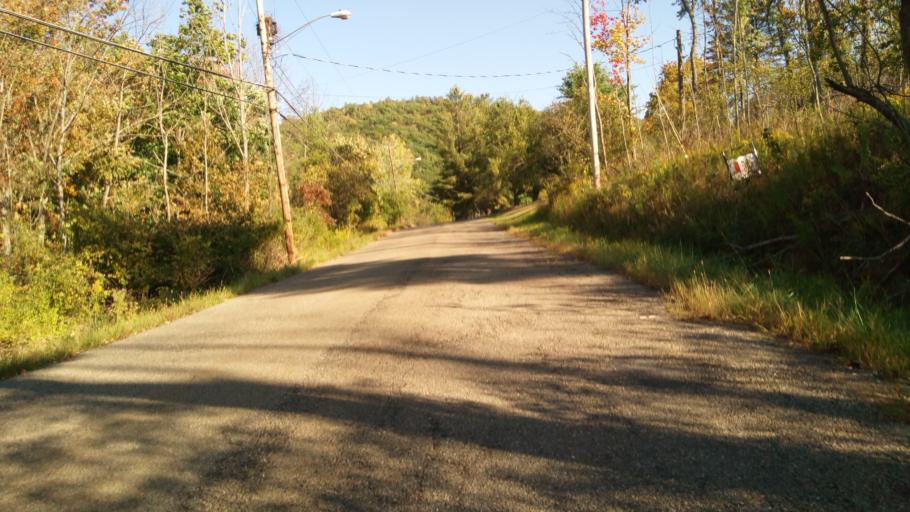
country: US
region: New York
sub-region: Chemung County
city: West Elmira
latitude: 42.0691
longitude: -76.8384
